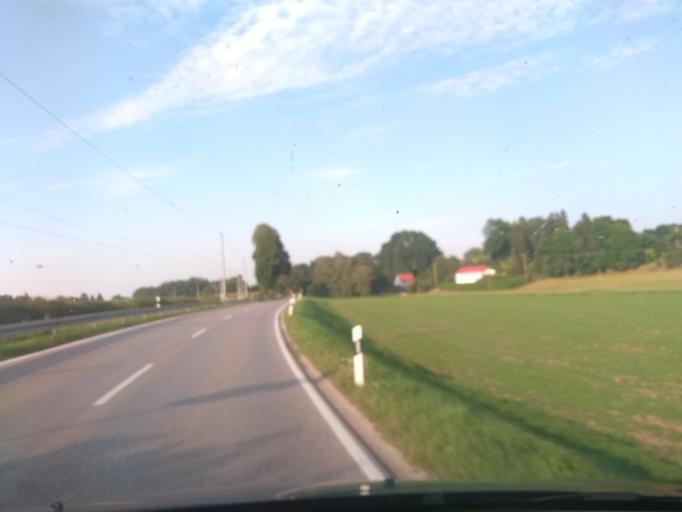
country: DE
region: Bavaria
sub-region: Upper Bavaria
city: Schwabhausen
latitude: 48.3128
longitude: 11.3851
